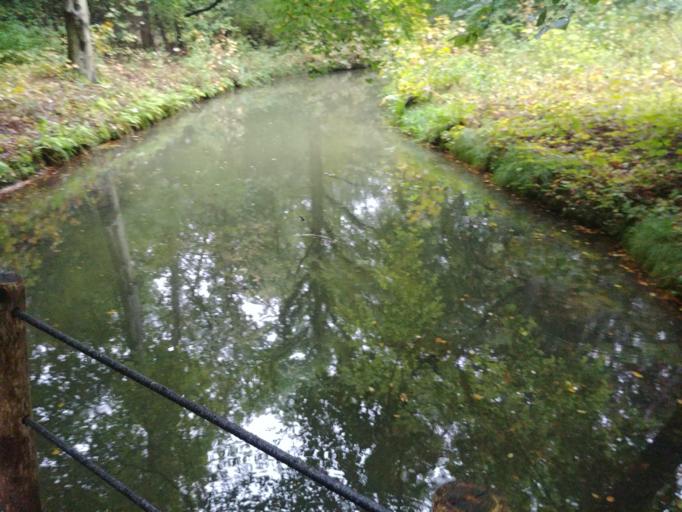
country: NL
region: North Holland
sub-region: Gemeente Bloemendaal
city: Bloemendaal
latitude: 52.3817
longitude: 4.5967
